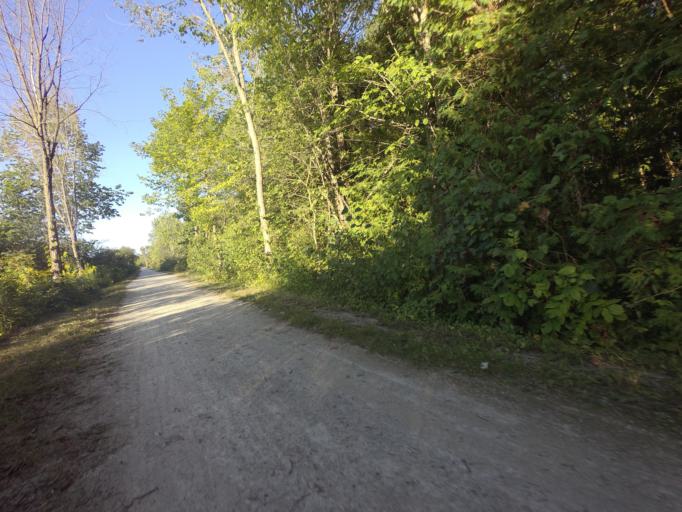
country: CA
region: Ontario
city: Orangeville
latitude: 43.8172
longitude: -79.9257
